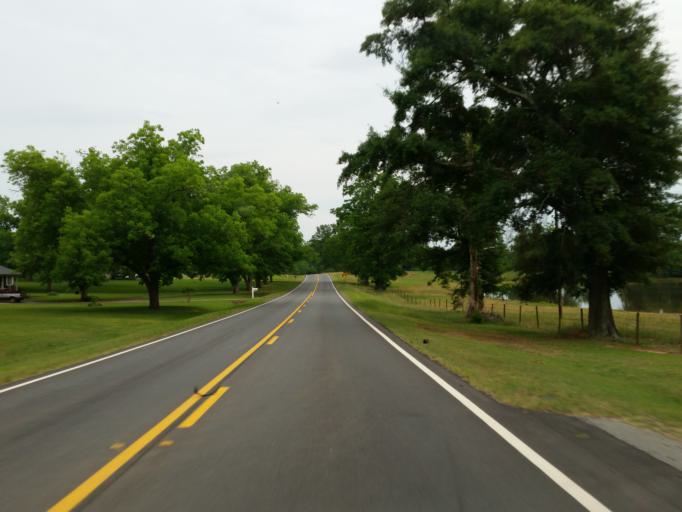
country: US
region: Georgia
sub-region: Dooly County
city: Unadilla
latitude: 32.3373
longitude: -83.7892
